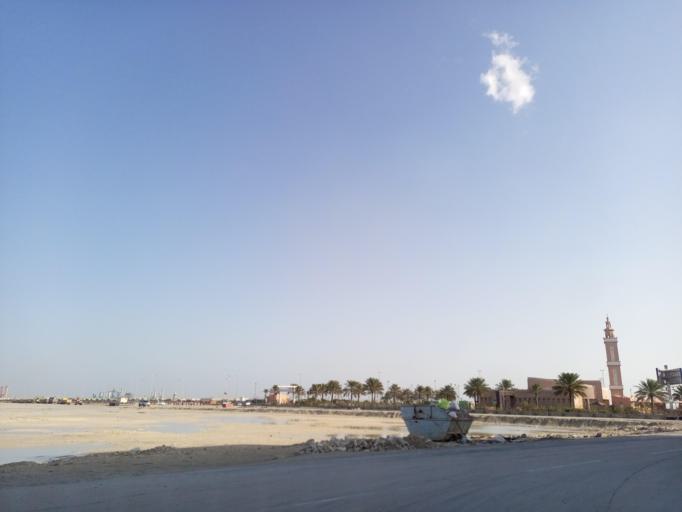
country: BH
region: Muharraq
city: Al Hadd
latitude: 26.2265
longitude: 50.6333
